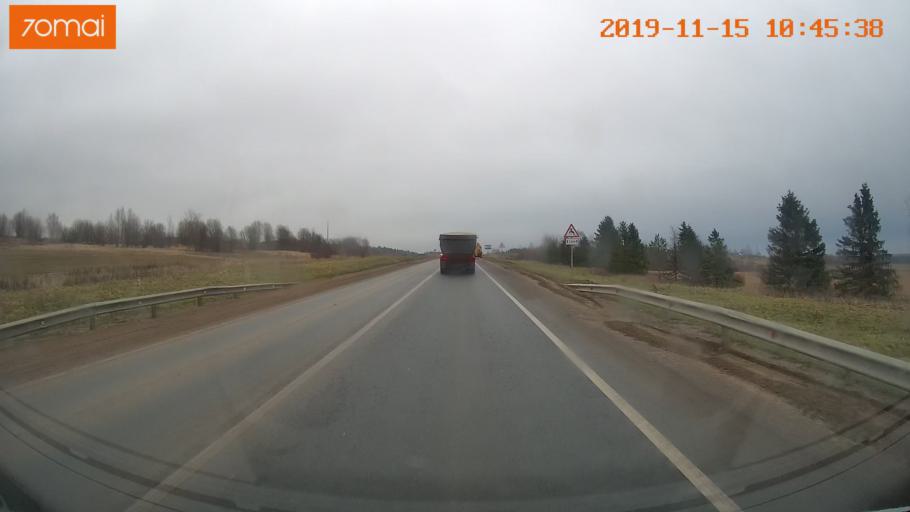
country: RU
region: Vologda
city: Sheksna
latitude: 59.2112
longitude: 38.5919
